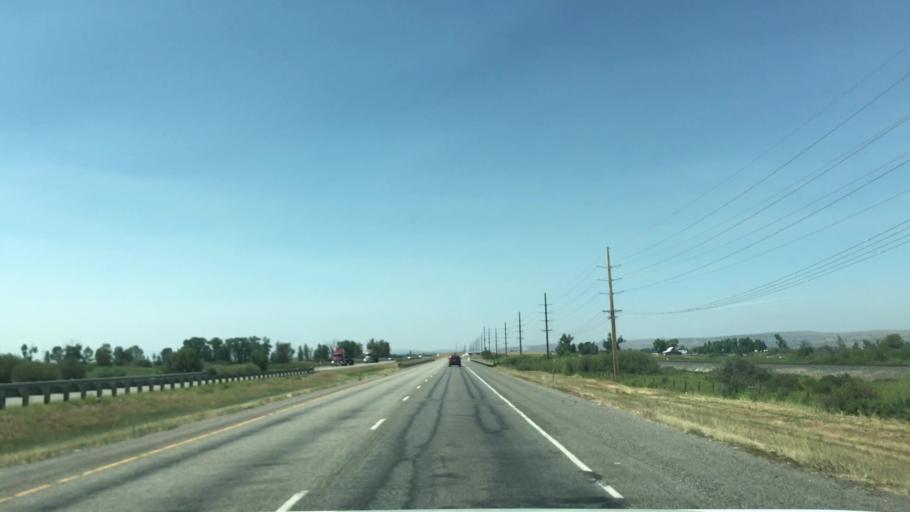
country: US
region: Montana
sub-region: Gallatin County
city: Manhattan
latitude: 45.8370
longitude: -111.2967
